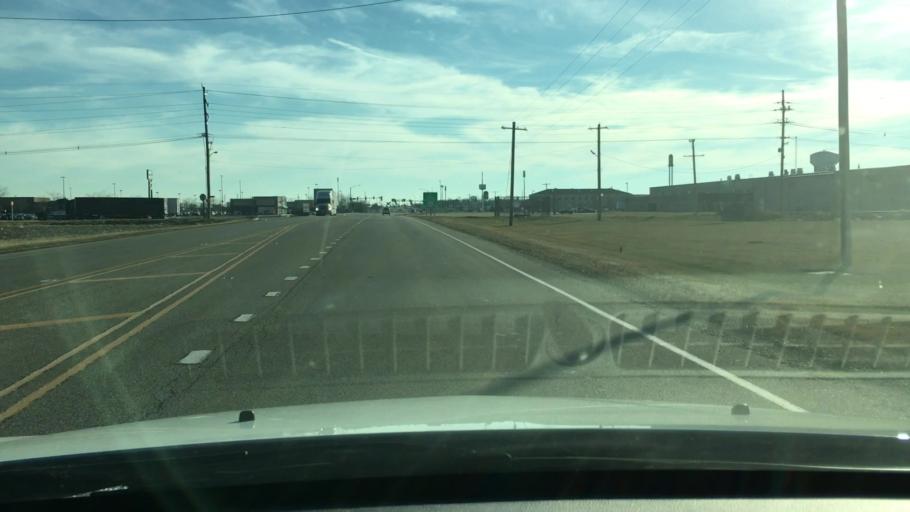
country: US
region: Illinois
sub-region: LaSalle County
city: Peru
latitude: 41.3756
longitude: -89.1256
